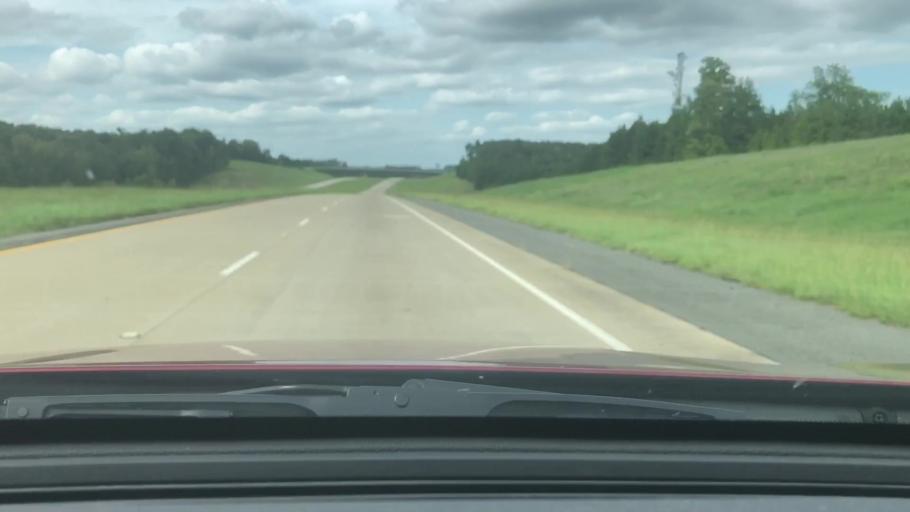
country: US
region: Louisiana
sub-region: Caddo Parish
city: Vivian
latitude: 32.9705
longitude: -93.9072
